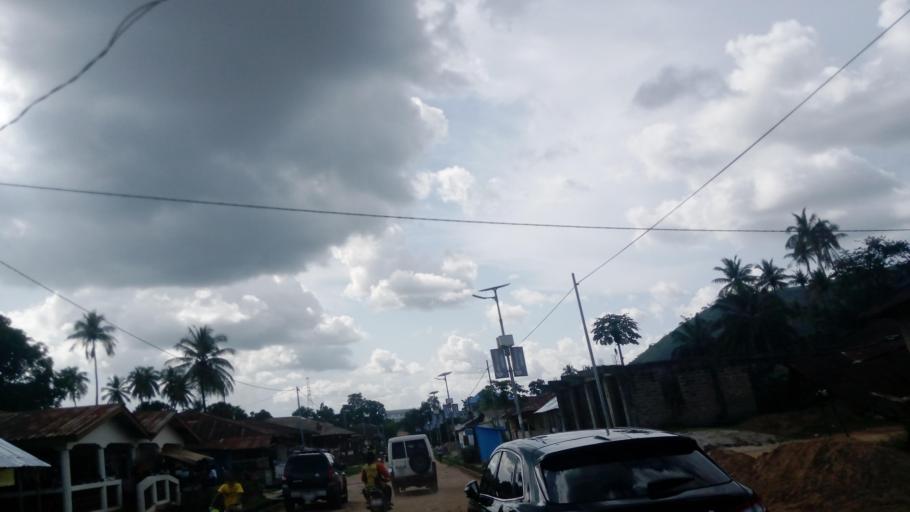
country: SL
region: Northern Province
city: Makeni
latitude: 8.8910
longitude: -12.0455
